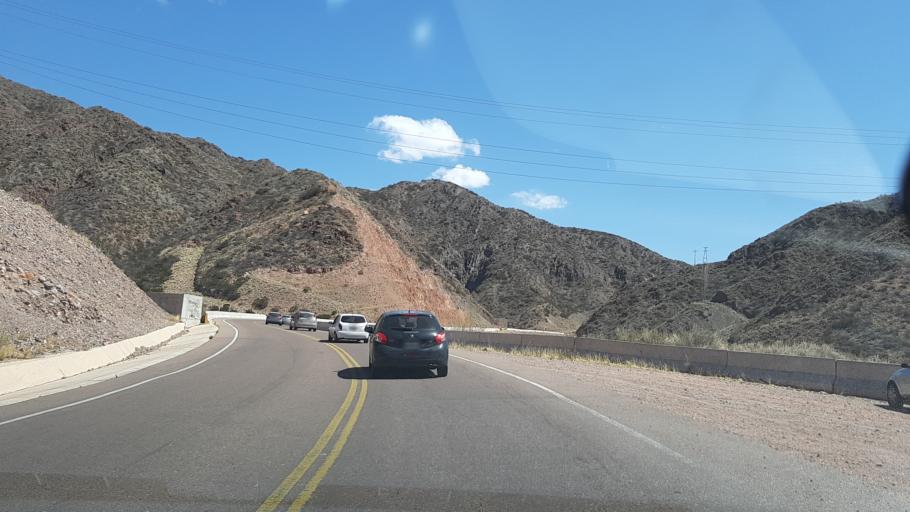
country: AR
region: Mendoza
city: Lujan de Cuyo
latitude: -32.9949
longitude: -69.1478
